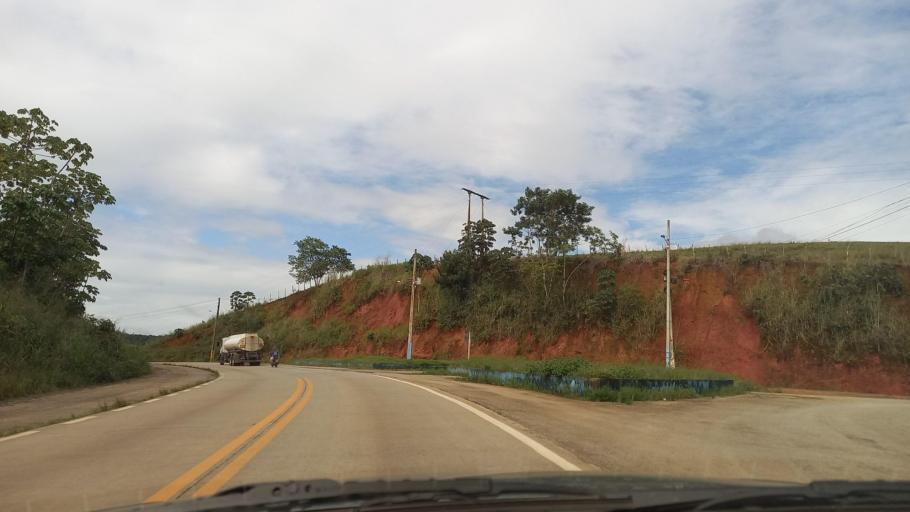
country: BR
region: Pernambuco
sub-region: Maraial
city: Maraial
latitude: -8.7498
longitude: -35.8083
